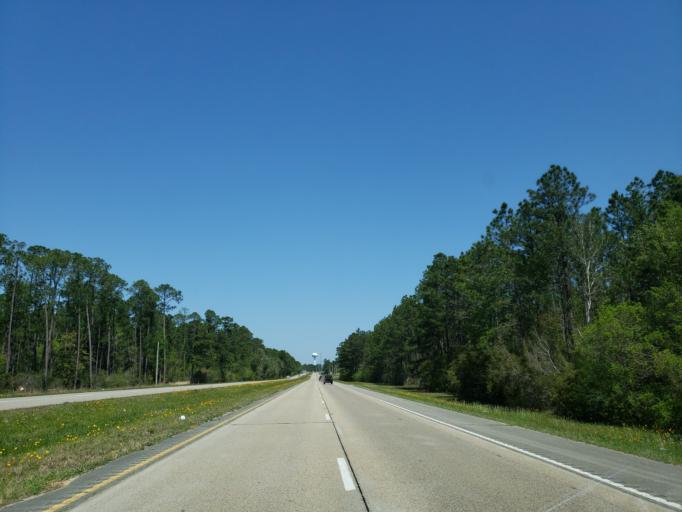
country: US
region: Mississippi
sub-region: Harrison County
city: Saucier
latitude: 30.5742
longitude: -89.1250
